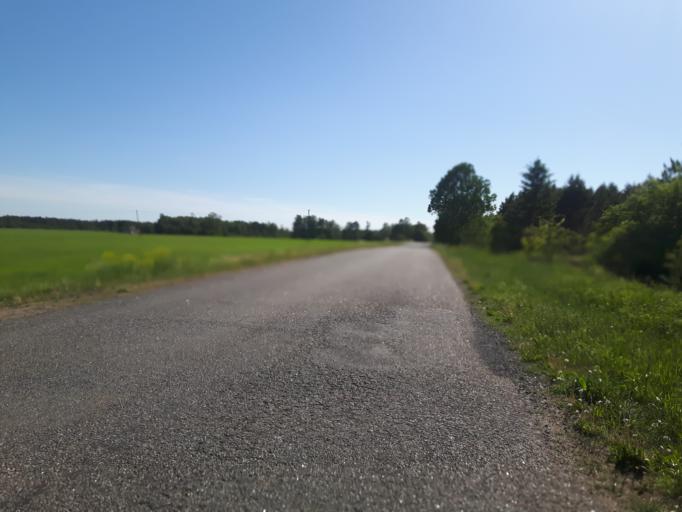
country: EE
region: Laeaene-Virumaa
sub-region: Haljala vald
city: Haljala
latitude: 59.5428
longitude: 26.1098
